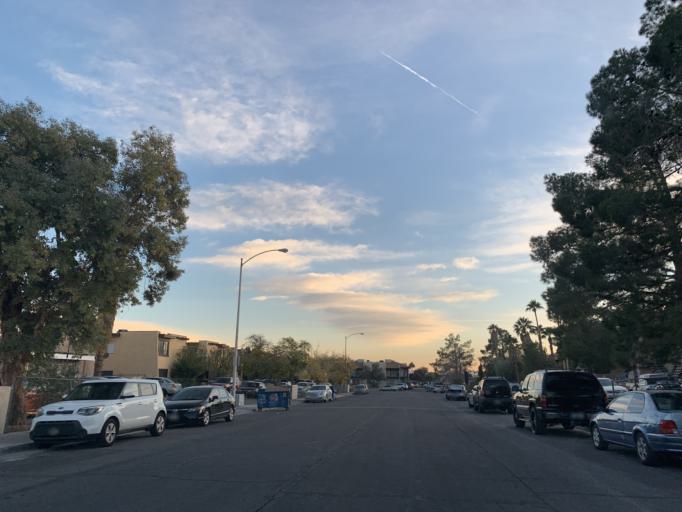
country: US
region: Nevada
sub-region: Clark County
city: Spring Valley
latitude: 36.1129
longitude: -115.2159
